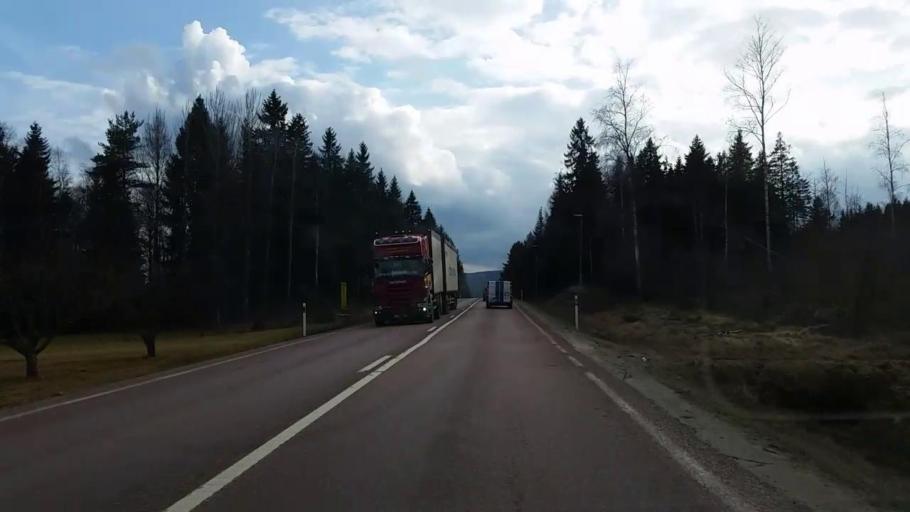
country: SE
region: Gaevleborg
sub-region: Ljusdals Kommun
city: Jaervsoe
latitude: 61.6870
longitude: 16.1481
